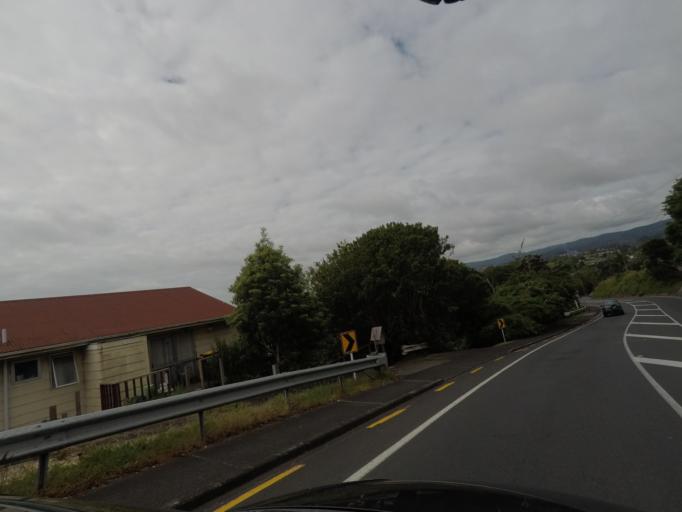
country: NZ
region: Auckland
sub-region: Auckland
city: Rosebank
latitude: -36.8558
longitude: 174.6116
